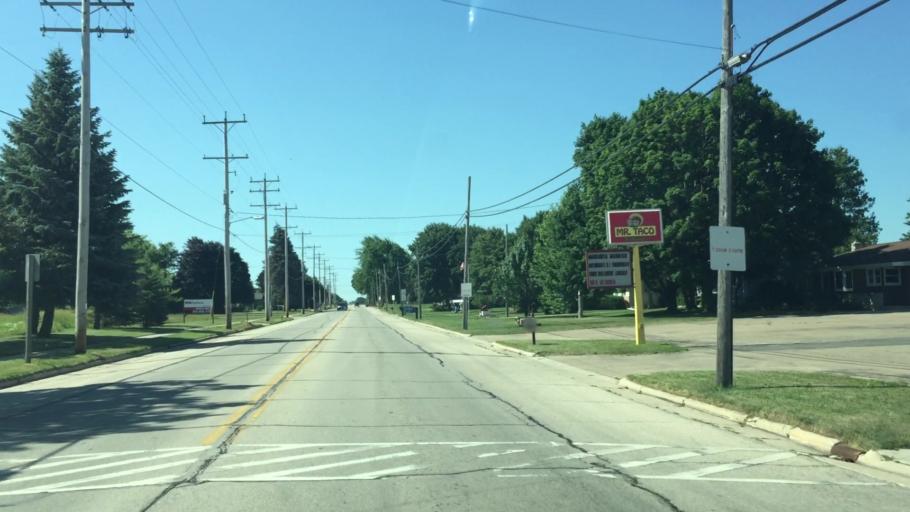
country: US
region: Wisconsin
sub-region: Calumet County
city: Hilbert
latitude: 44.1380
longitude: -88.1641
